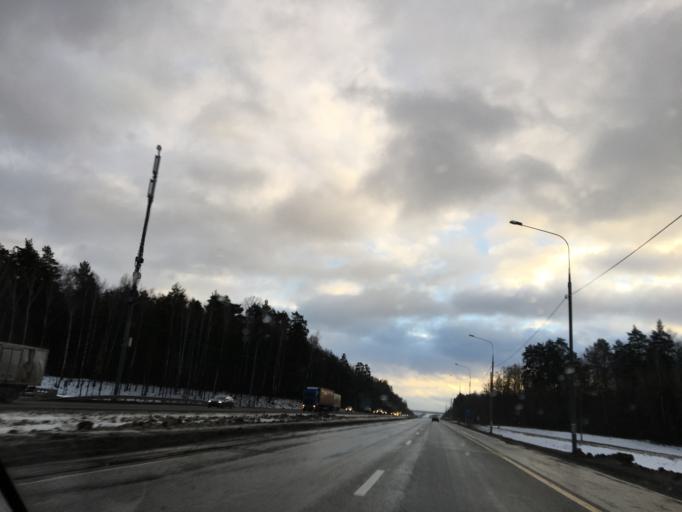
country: RU
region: Moskovskaya
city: Danki
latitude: 54.9053
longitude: 37.5116
